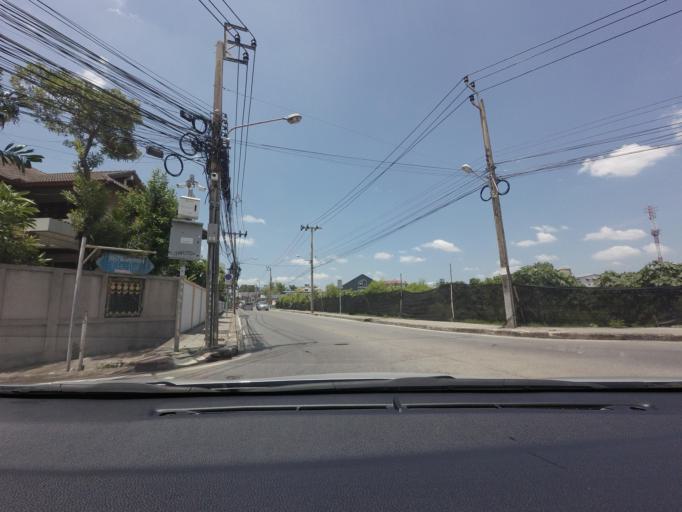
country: TH
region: Bangkok
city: Suan Luang
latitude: 13.7041
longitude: 100.6368
